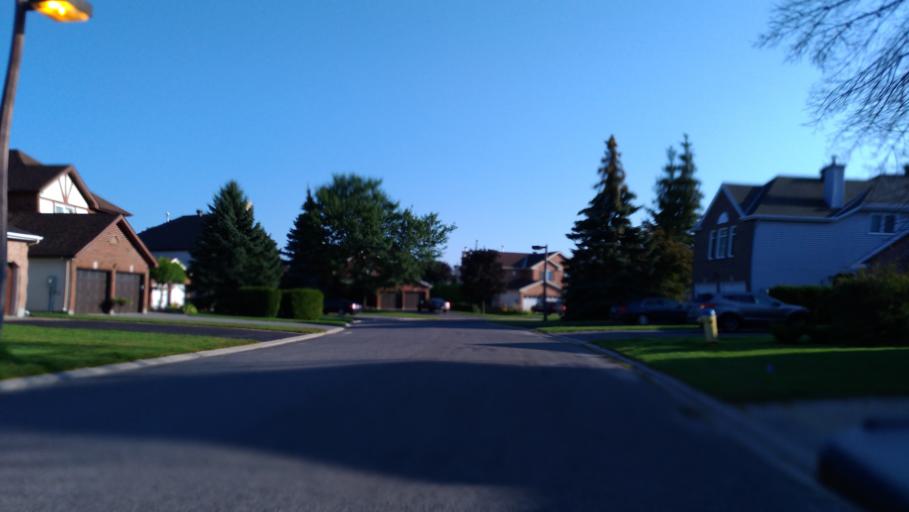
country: CA
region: Ontario
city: Bells Corners
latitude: 45.3469
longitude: -75.9348
